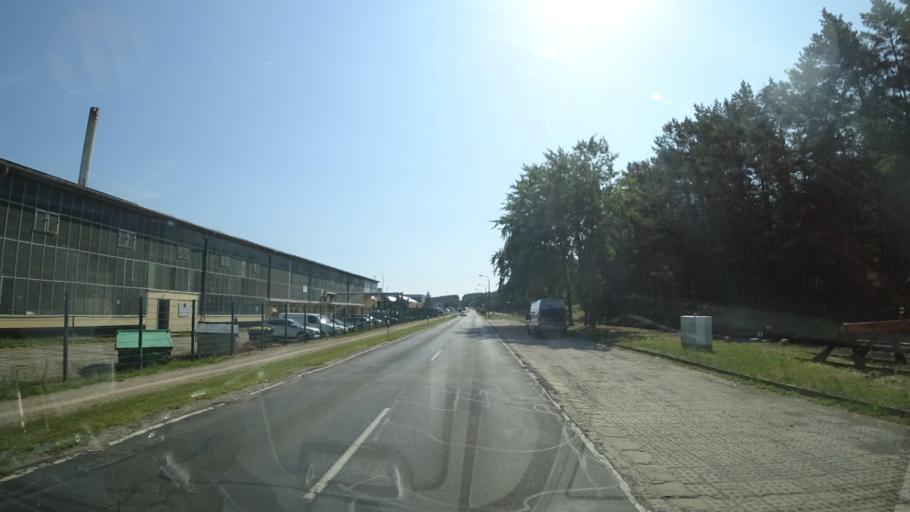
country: DE
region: Mecklenburg-Vorpommern
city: Lubmin
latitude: 54.1376
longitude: 13.6640
